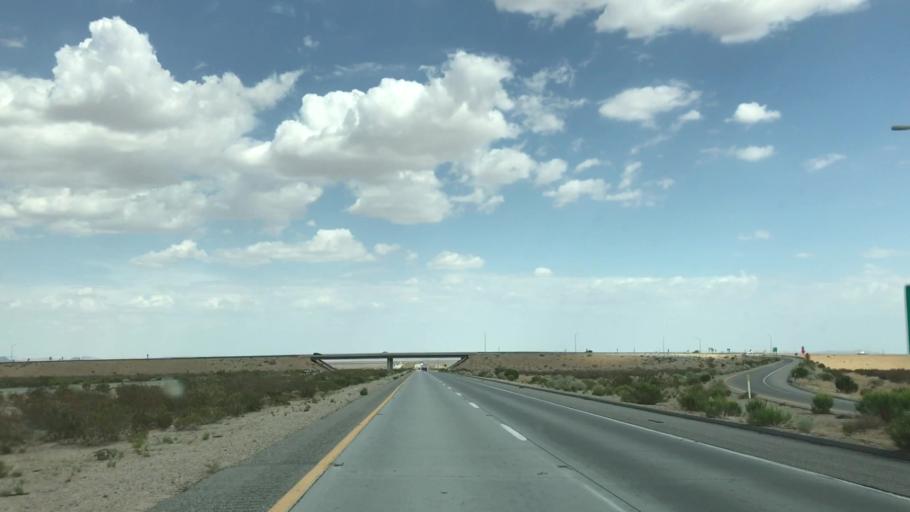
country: US
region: California
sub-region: Kern County
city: Mojave
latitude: 35.1010
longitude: -118.1493
